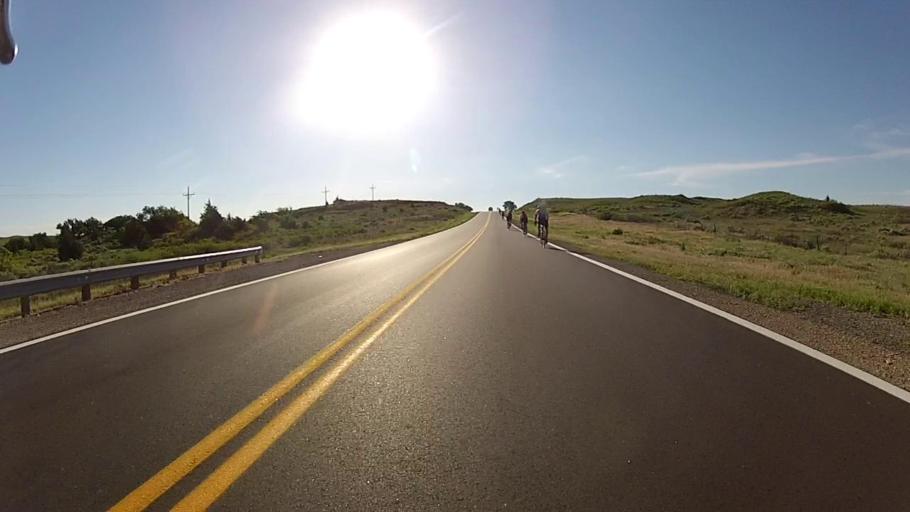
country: US
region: Kansas
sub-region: Comanche County
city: Coldwater
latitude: 37.2809
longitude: -99.0325
